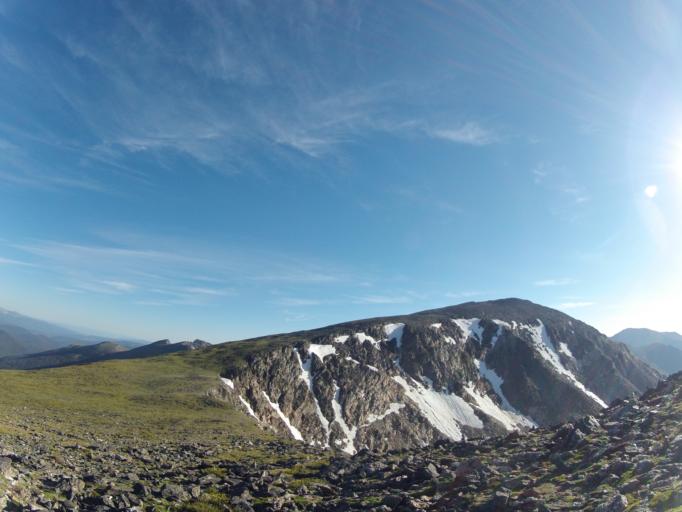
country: US
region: Colorado
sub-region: Larimer County
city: Estes Park
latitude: 40.4462
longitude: -105.6909
